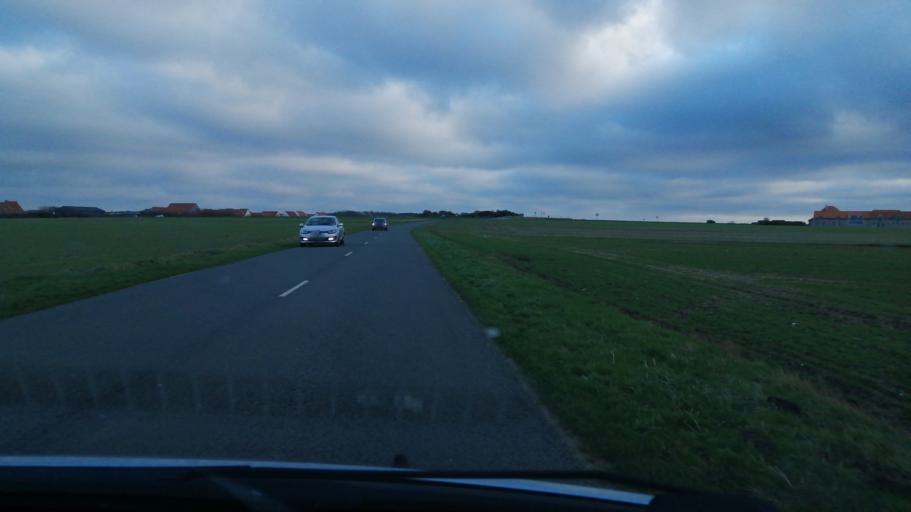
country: FR
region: Nord-Pas-de-Calais
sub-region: Departement du Pas-de-Calais
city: Ambleteuse
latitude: 50.8492
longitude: 1.6025
